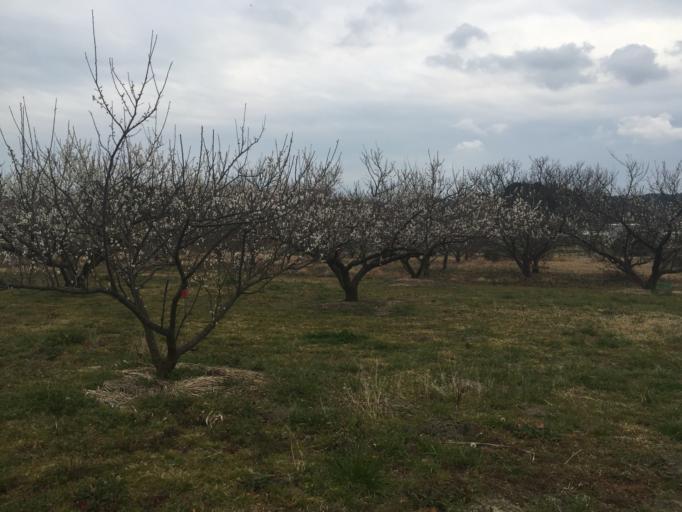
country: JP
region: Shizuoka
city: Kakegawa
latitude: 34.7904
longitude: 138.0631
